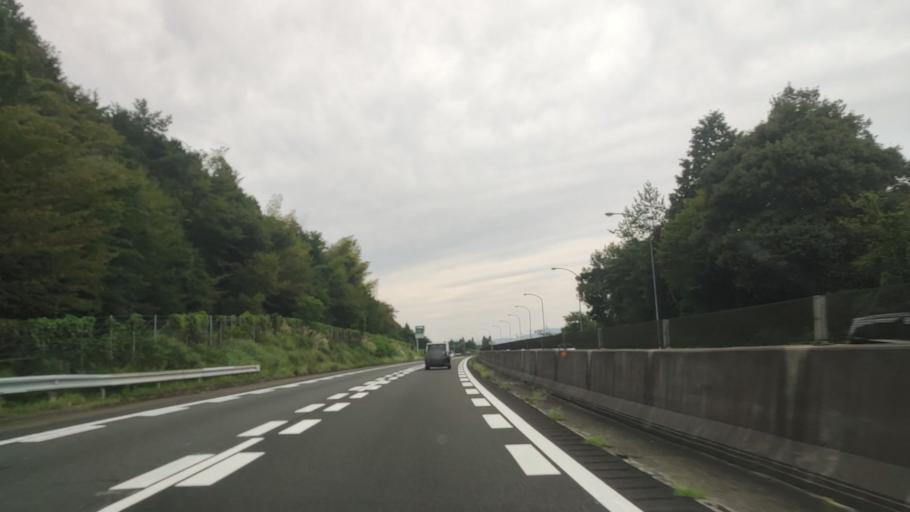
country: JP
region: Shiga Prefecture
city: Hikone
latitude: 35.1738
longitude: 136.2786
